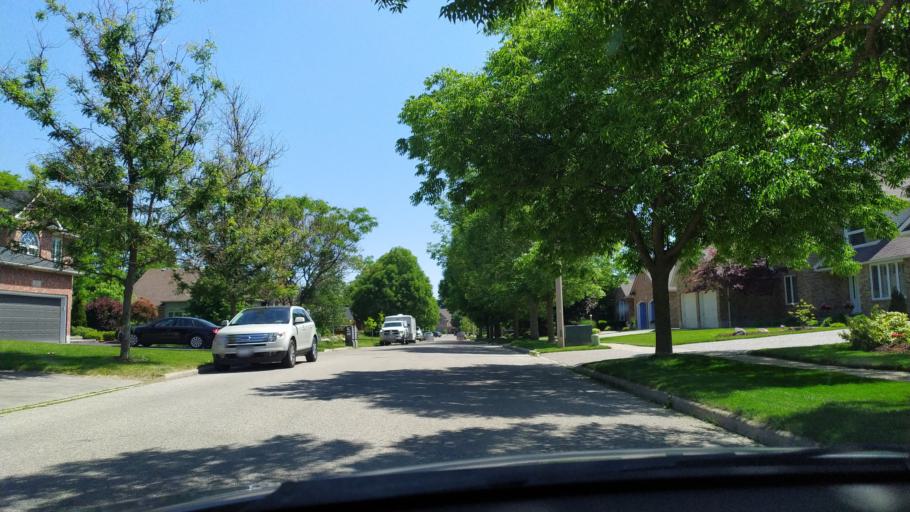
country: CA
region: Ontario
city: Waterloo
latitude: 43.4521
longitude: -80.5696
